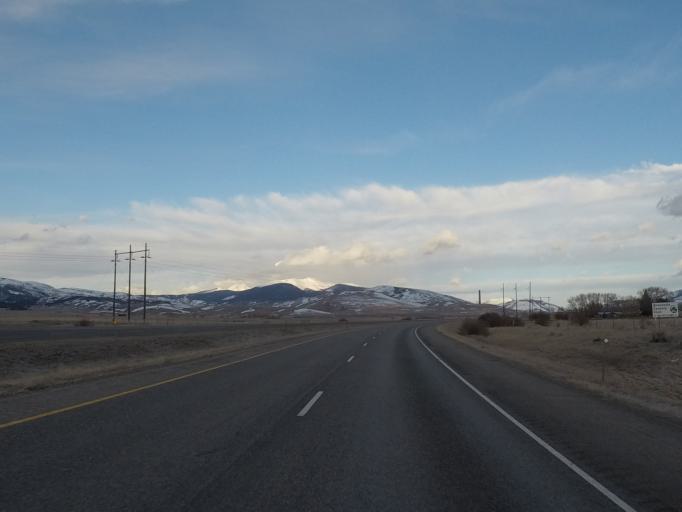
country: US
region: Montana
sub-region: Deer Lodge County
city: Warm Springs
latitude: 46.0958
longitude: -112.8208
